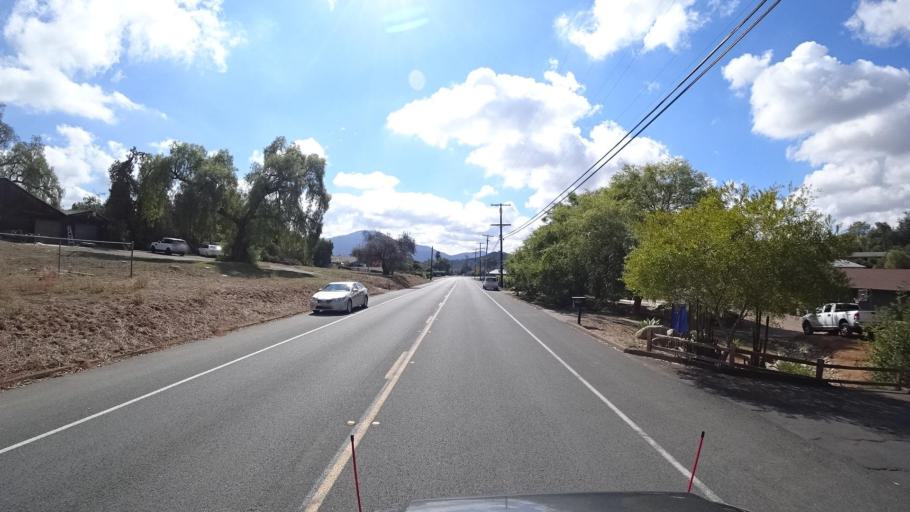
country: US
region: California
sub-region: San Diego County
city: Rancho San Diego
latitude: 32.7643
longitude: -116.9415
